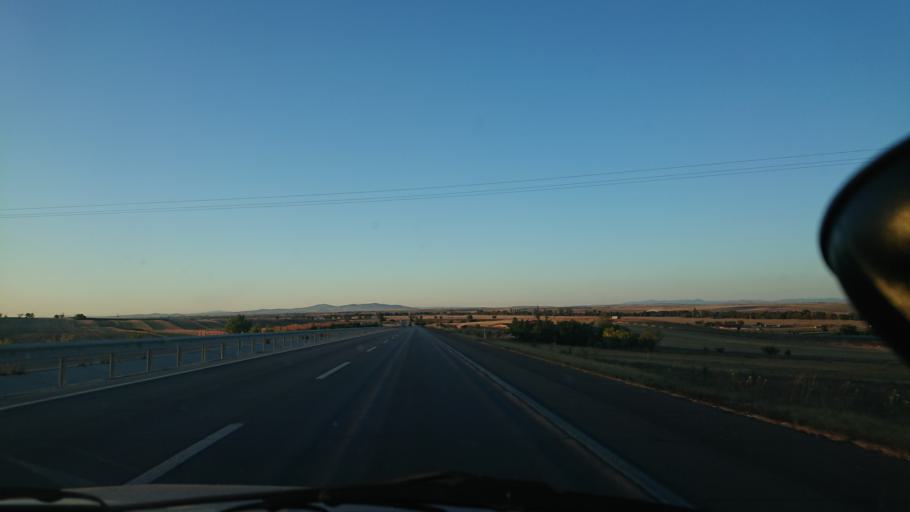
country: TR
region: Eskisehir
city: Mahmudiye
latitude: 39.5114
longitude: 30.9645
